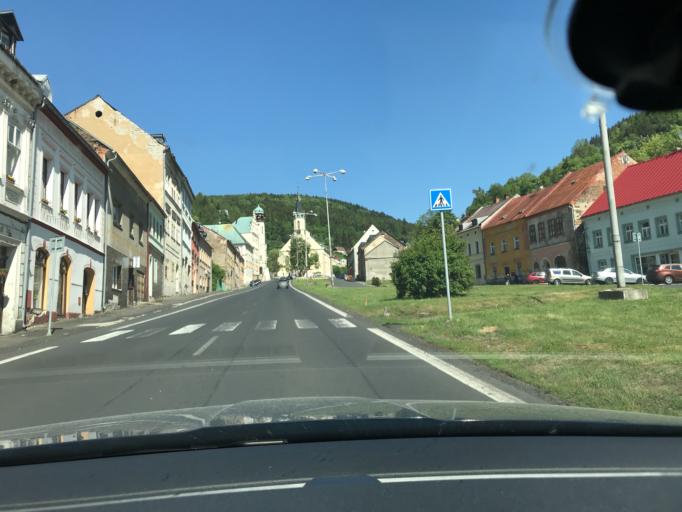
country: CZ
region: Karlovarsky
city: Jachymov
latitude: 50.3698
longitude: 12.9160
